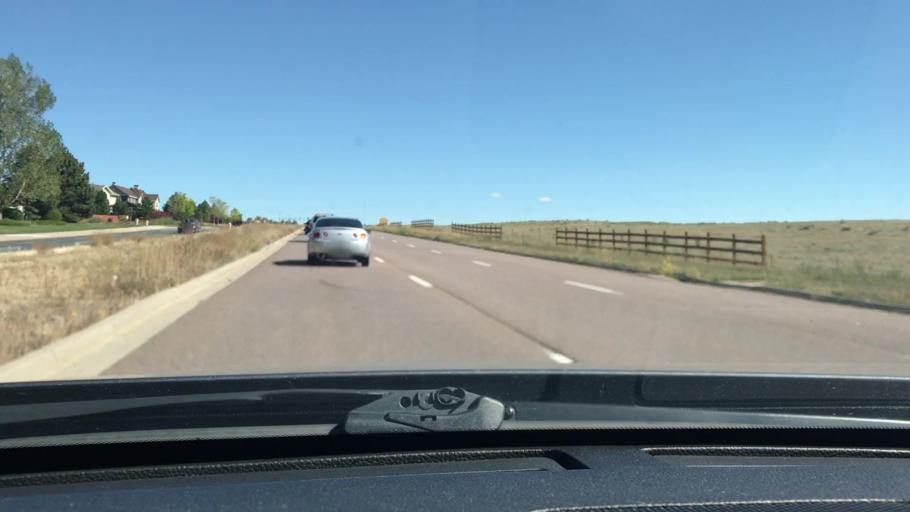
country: US
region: Colorado
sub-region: Arapahoe County
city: Dove Valley
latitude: 39.6384
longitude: -104.7459
